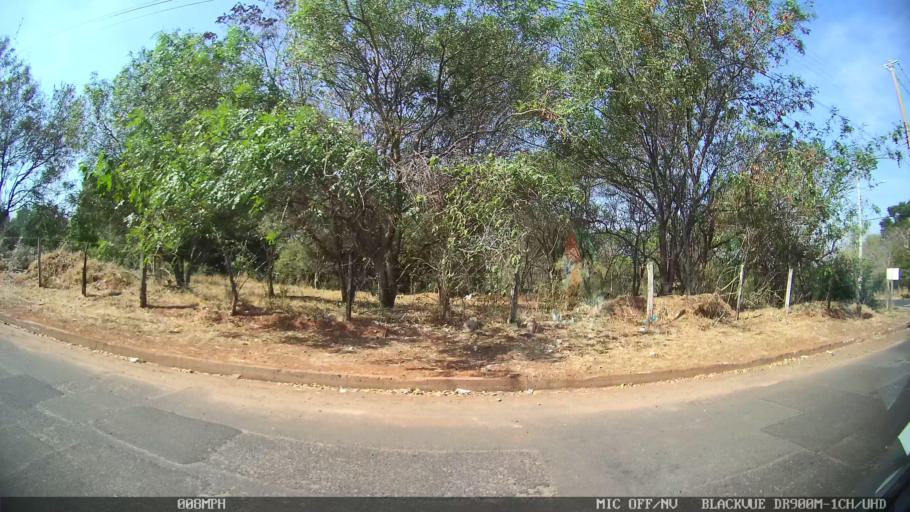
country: BR
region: Sao Paulo
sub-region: Sao Jose Do Rio Preto
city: Sao Jose do Rio Preto
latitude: -20.7887
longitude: -49.4364
